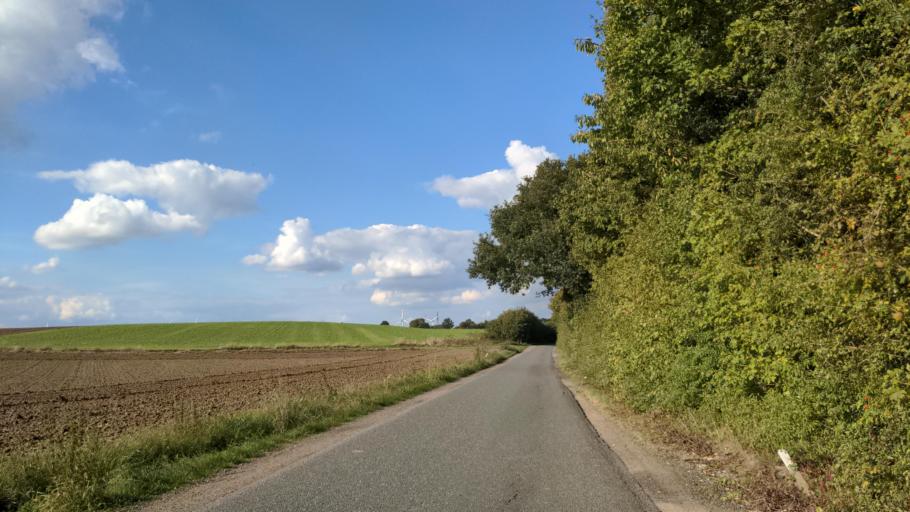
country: DE
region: Schleswig-Holstein
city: Monkhagen
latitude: 53.9073
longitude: 10.5926
